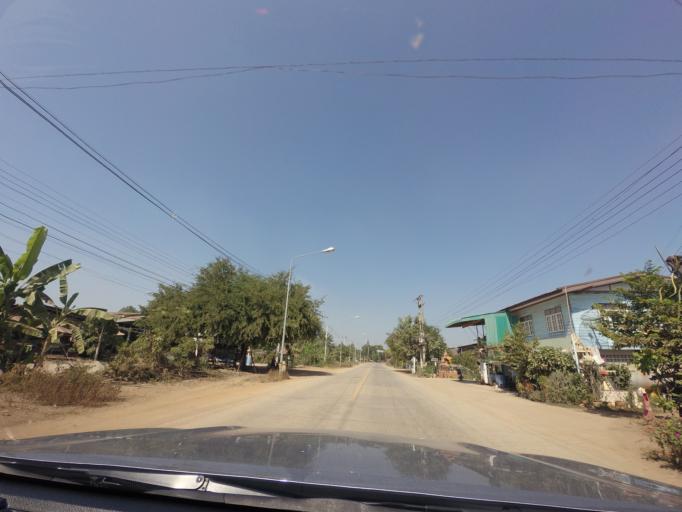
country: TH
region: Sukhothai
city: Sawankhalok
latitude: 17.2453
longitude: 99.7744
